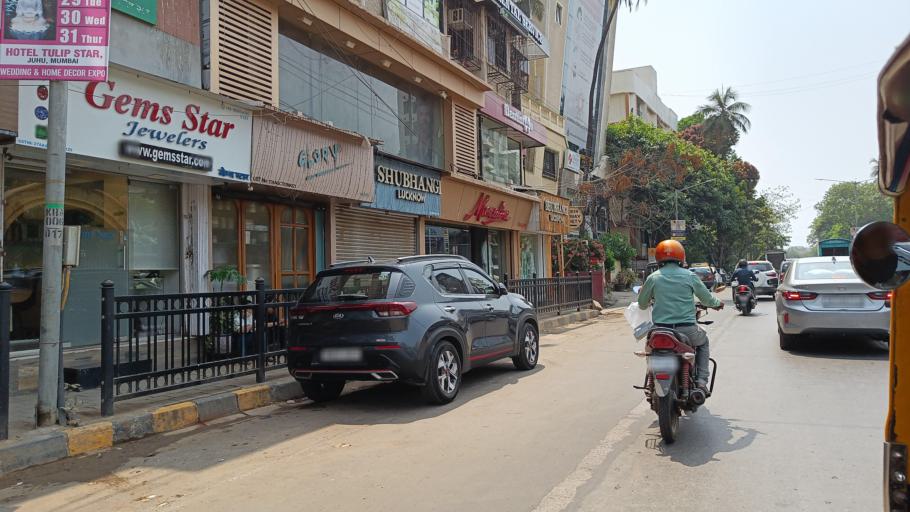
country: IN
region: Maharashtra
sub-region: Mumbai Suburban
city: Mumbai
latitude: 19.1021
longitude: 72.8270
